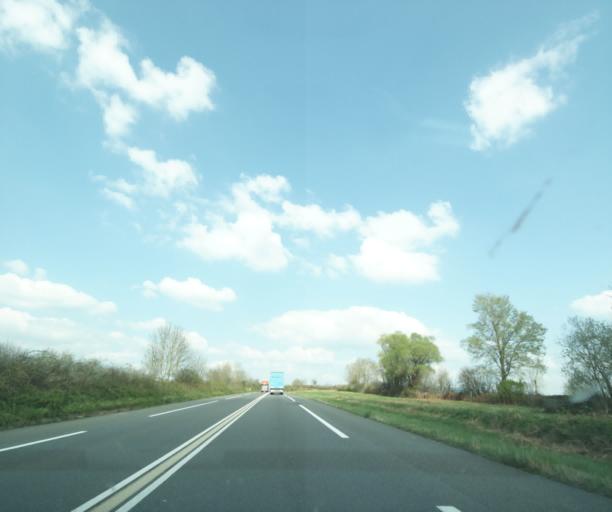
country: FR
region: Auvergne
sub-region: Departement de l'Allier
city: Montmarault
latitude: 46.3446
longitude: 2.9894
